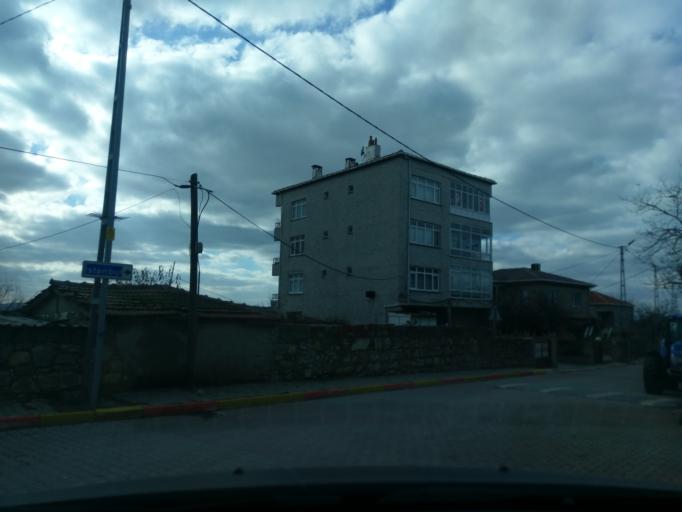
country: TR
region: Istanbul
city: Durusu
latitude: 41.3172
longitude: 28.7213
